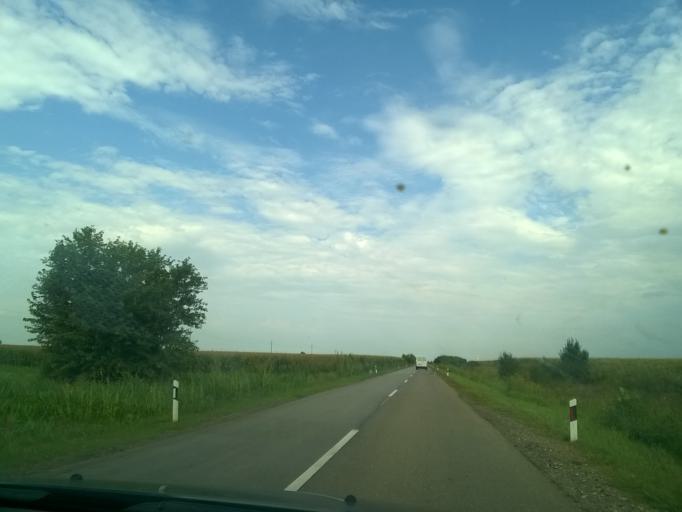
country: RS
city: Stajicevo
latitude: 45.2985
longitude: 20.4937
